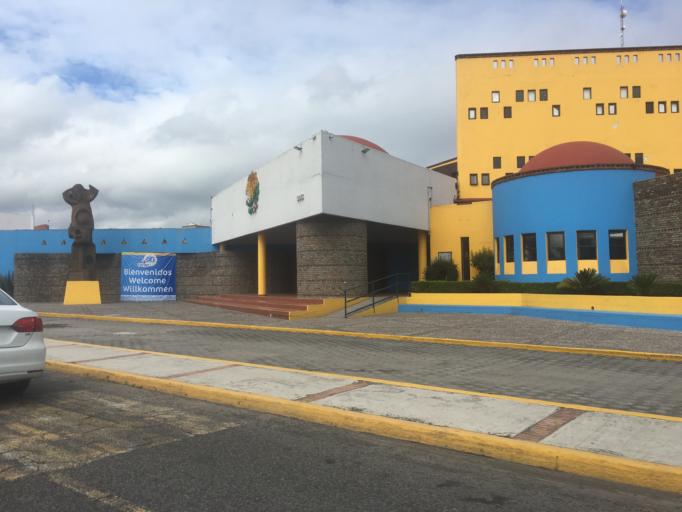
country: MX
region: Morelos
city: Metepec
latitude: 19.2638
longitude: -99.6077
